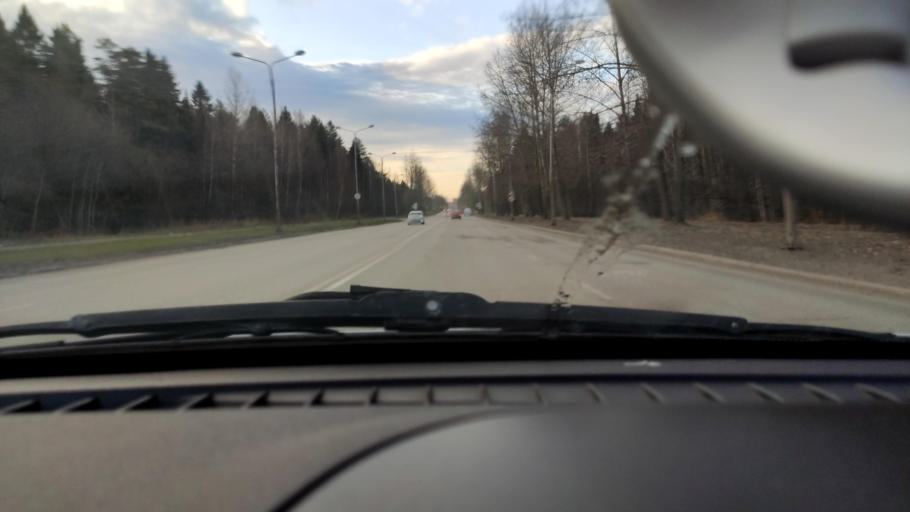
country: RU
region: Perm
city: Perm
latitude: 58.0877
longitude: 56.3798
